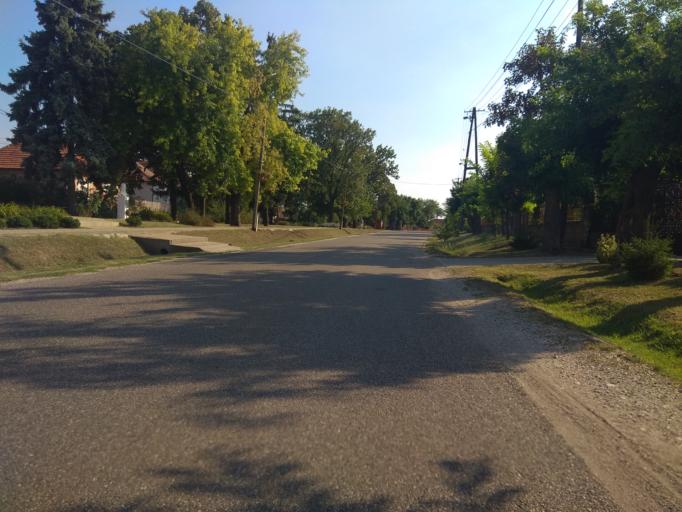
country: HU
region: Borsod-Abauj-Zemplen
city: Mezokeresztes
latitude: 47.8574
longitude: 20.6790
